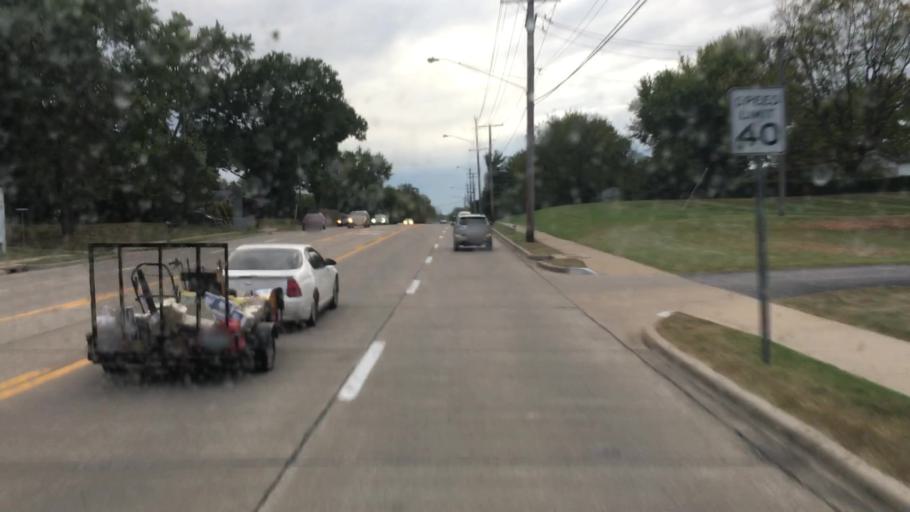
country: US
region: Missouri
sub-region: Saint Louis County
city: Florissant
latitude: 38.8253
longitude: -90.3363
